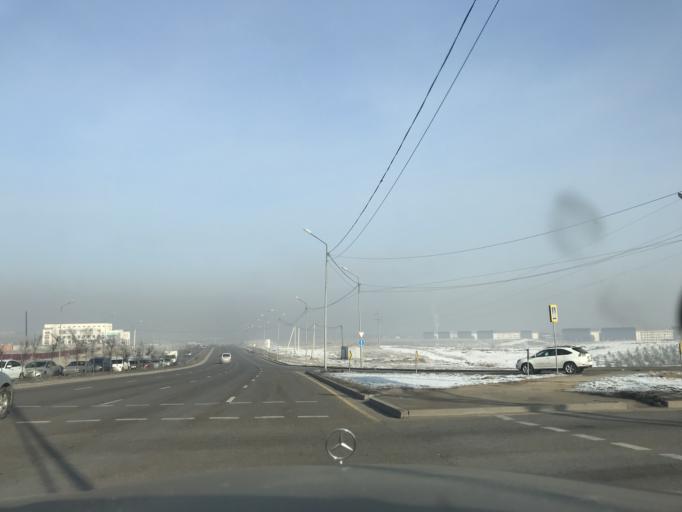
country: KZ
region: Almaty Oblysy
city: Burunday
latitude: 43.3134
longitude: 76.8341
